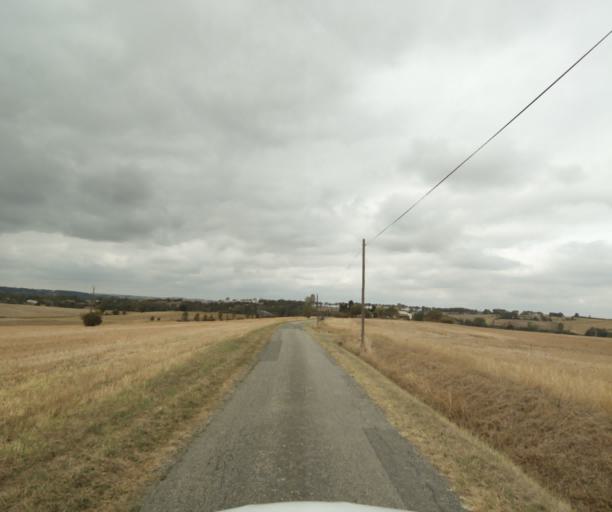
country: FR
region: Midi-Pyrenees
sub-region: Departement de la Haute-Garonne
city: Villefranche-de-Lauragais
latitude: 43.4103
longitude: 1.7287
